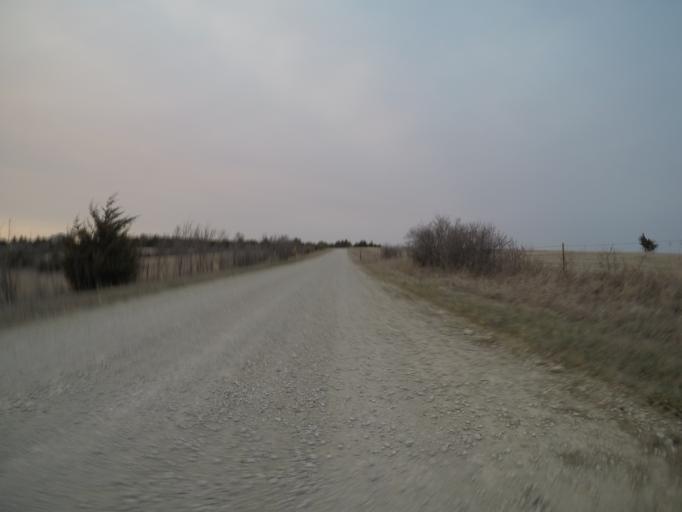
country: US
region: Kansas
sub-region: Riley County
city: Manhattan
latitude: 39.2369
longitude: -96.6513
